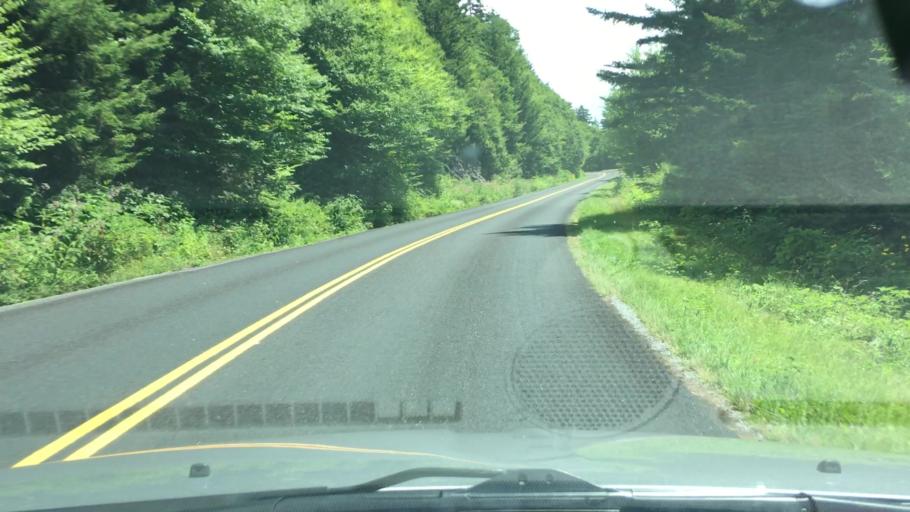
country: US
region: North Carolina
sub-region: Buncombe County
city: Black Mountain
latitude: 35.7445
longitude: -82.3294
